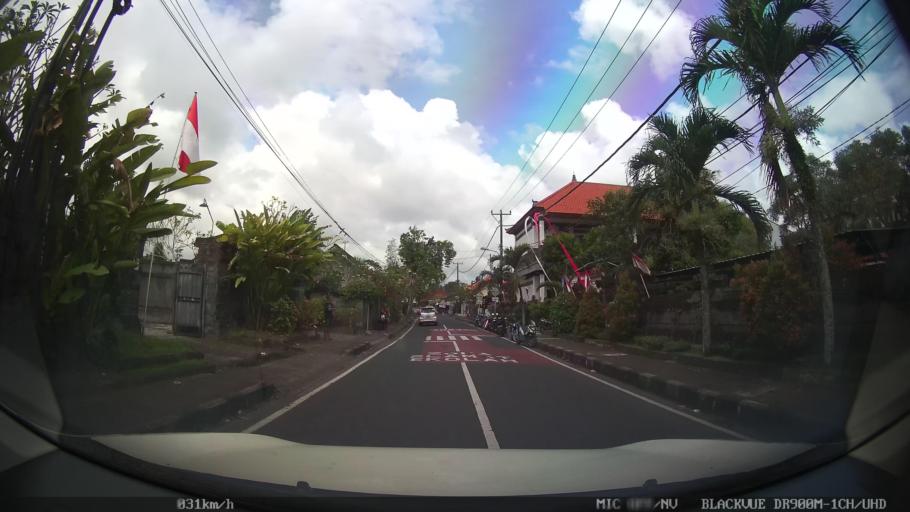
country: ID
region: Bali
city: Banjar Pekenjelodan
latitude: -8.5804
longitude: 115.1884
